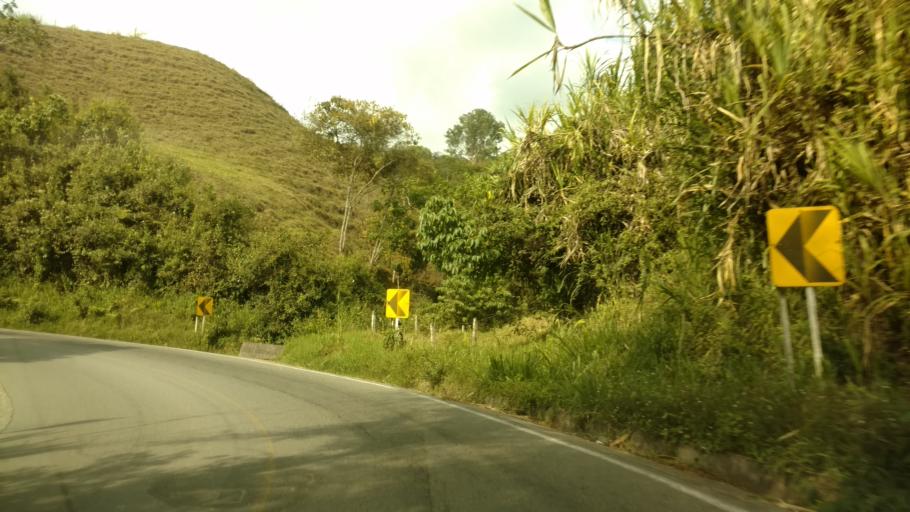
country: CO
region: Caldas
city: Neira
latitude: 5.1465
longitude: -75.5099
